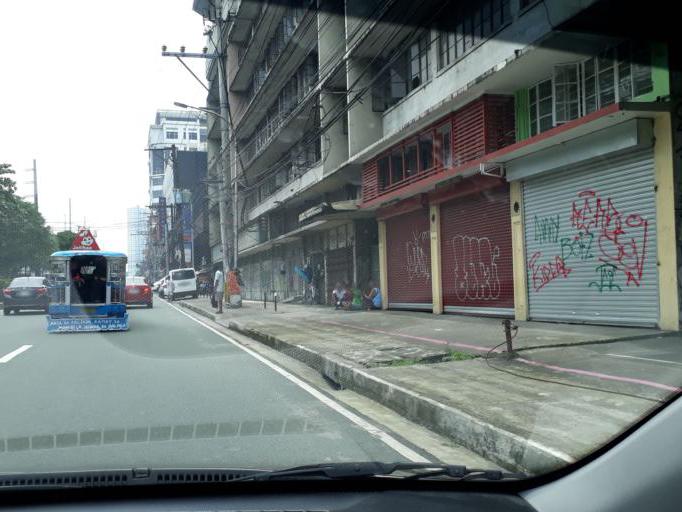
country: PH
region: Calabarzon
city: Del Monte
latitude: 14.6187
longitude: 121.0122
